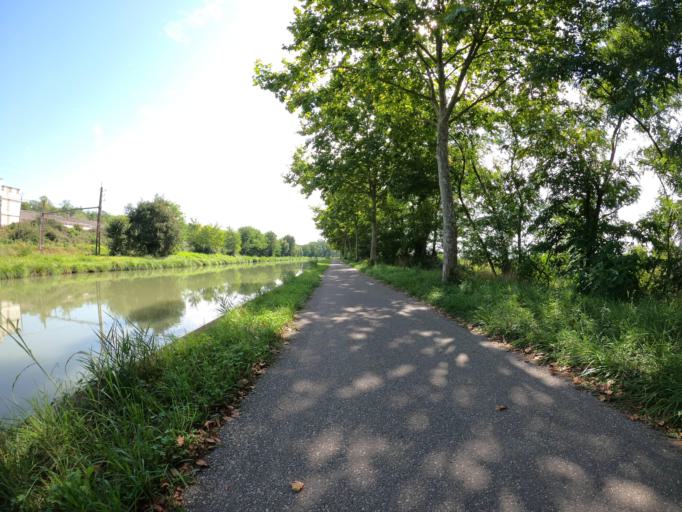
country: FR
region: Midi-Pyrenees
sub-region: Departement du Tarn-et-Garonne
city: Grisolles
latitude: 43.8630
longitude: 1.2772
